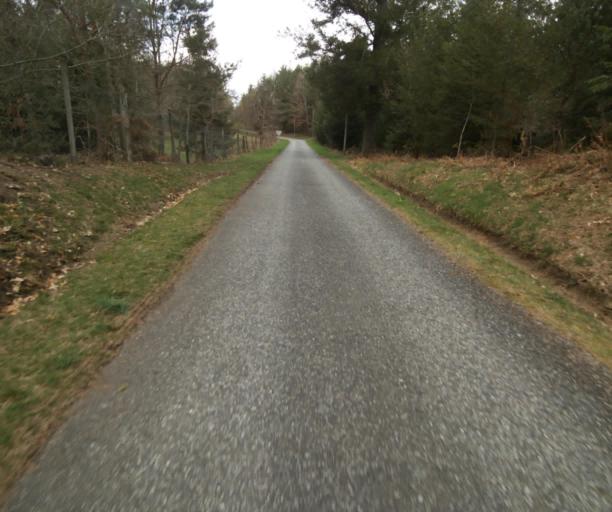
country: FR
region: Limousin
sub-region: Departement de la Correze
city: Correze
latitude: 45.2813
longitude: 1.9306
